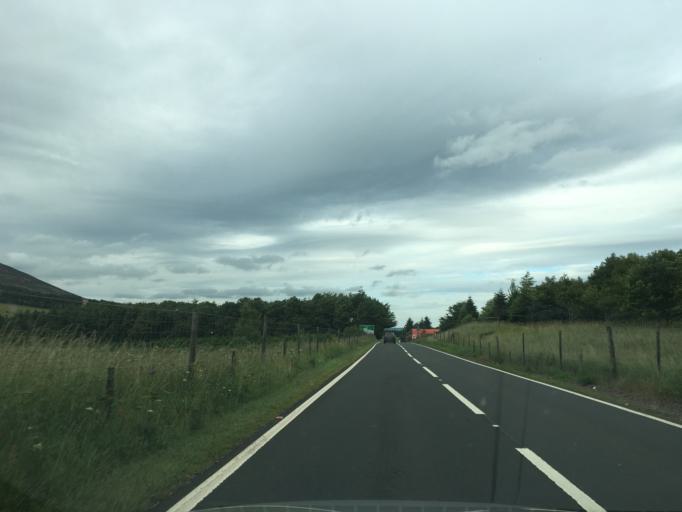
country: GB
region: Scotland
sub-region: South Lanarkshire
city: Biggar
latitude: 55.6806
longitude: -3.4572
